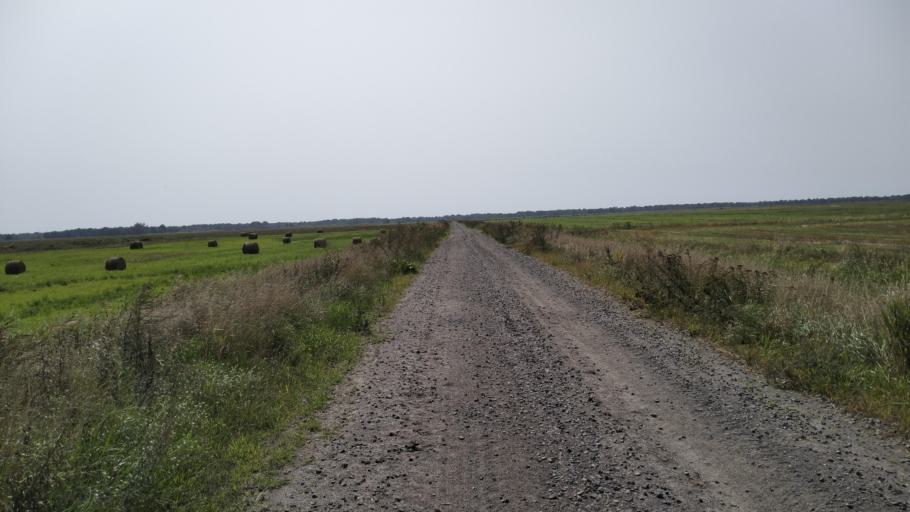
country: BY
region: Brest
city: Davyd-Haradok
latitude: 51.9885
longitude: 27.1757
